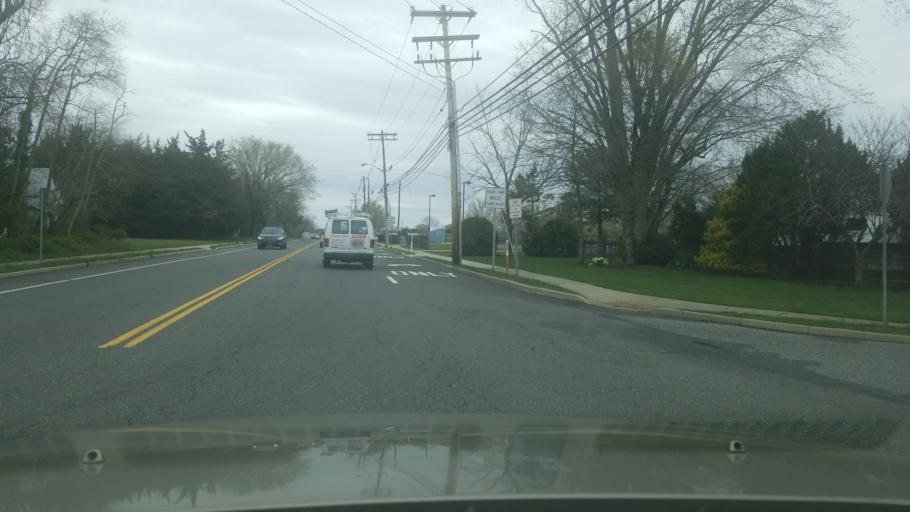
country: US
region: New Jersey
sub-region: Ocean County
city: Toms River
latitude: 39.9804
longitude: -74.1976
